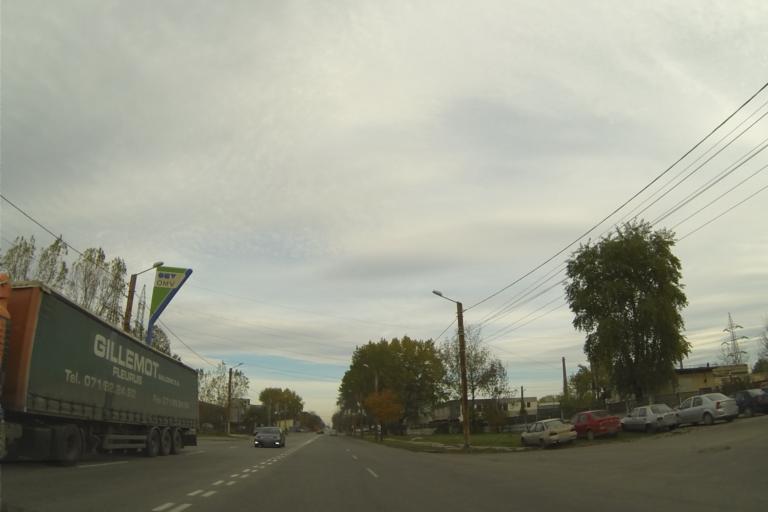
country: RO
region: Olt
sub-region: Municipiul Slatina
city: Slatina
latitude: 44.4431
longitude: 24.3777
